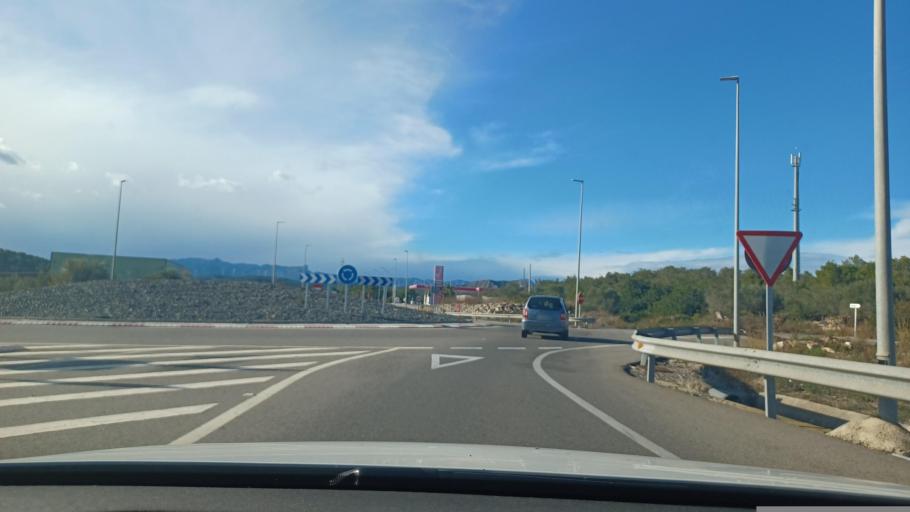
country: ES
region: Catalonia
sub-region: Provincia de Tarragona
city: El Perello
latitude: 40.8967
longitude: 0.7513
